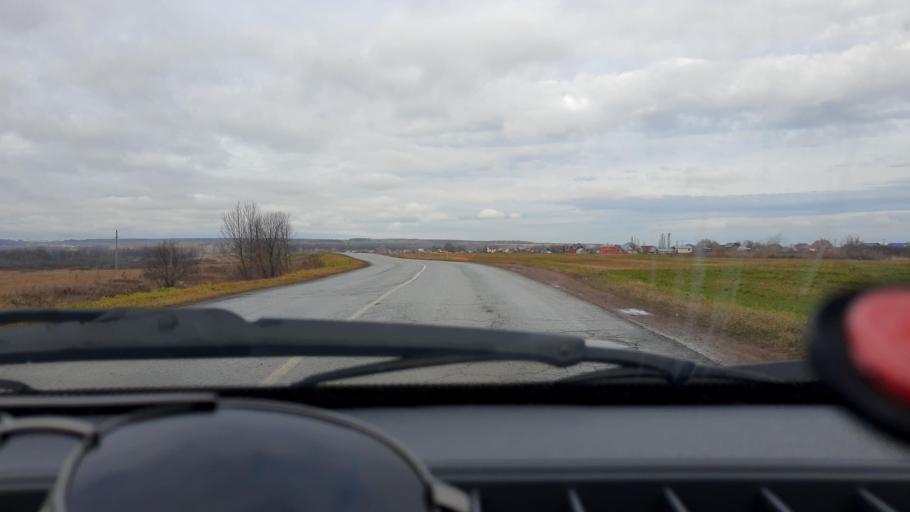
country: RU
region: Bashkortostan
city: Mikhaylovka
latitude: 54.8290
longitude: 55.9658
